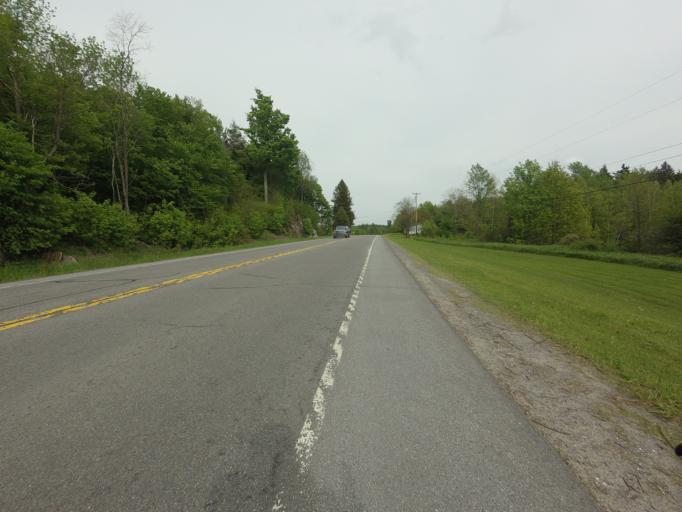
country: US
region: New York
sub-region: St. Lawrence County
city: Gouverneur
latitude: 44.3158
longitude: -75.2399
